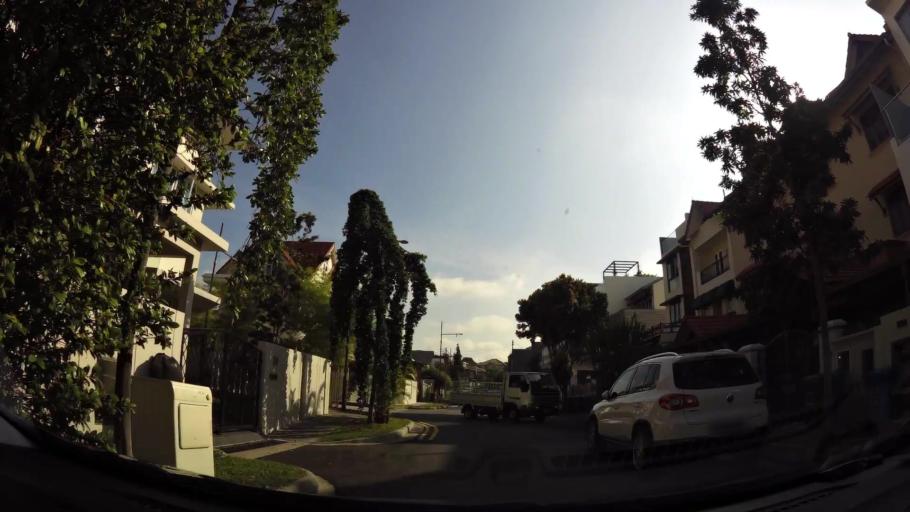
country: SG
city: Singapore
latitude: 1.3162
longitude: 103.9275
